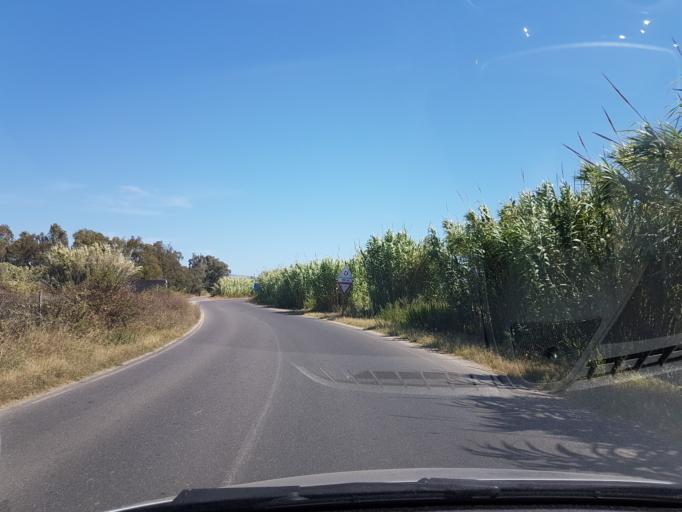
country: IT
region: Sardinia
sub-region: Provincia di Oristano
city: Cabras
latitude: 39.9212
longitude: 8.5358
